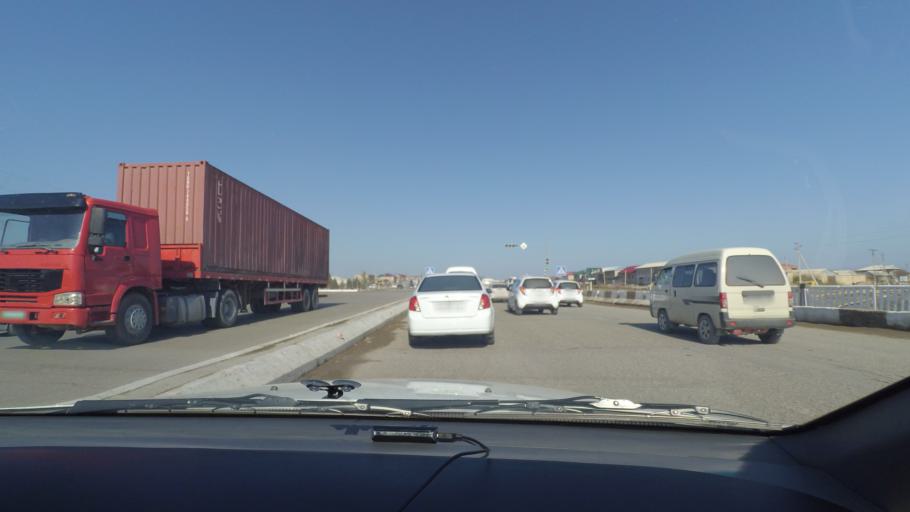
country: UZ
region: Bukhara
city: Bukhara
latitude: 39.8081
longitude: 64.4196
